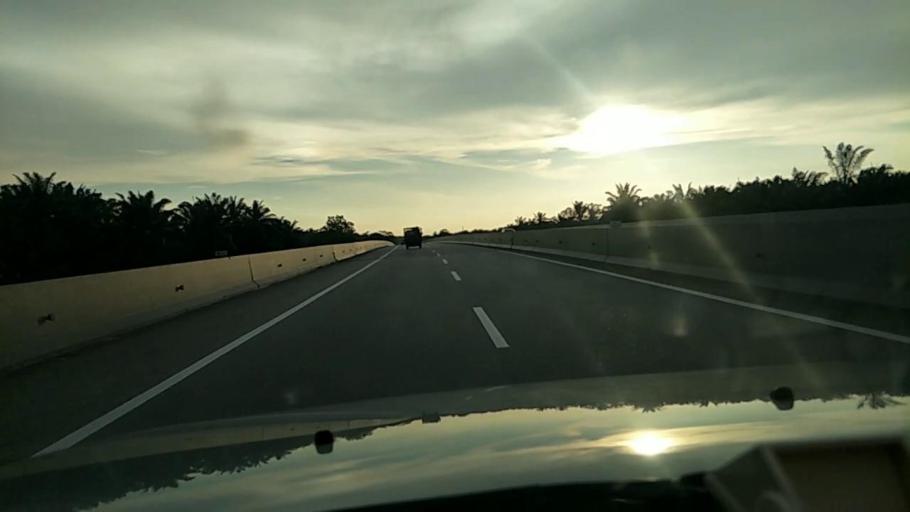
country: MY
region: Selangor
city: Batu Arang
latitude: 3.2886
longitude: 101.4326
